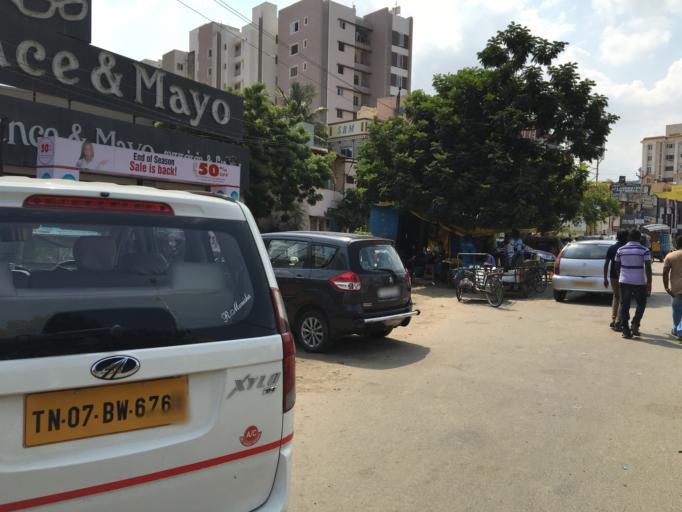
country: IN
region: Tamil Nadu
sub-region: Kancheepuram
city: Alandur
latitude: 12.9811
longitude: 80.2181
